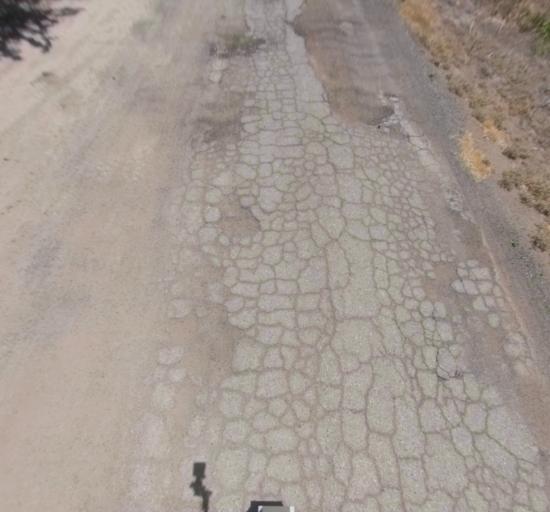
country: US
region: California
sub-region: Madera County
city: Chowchilla
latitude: 36.9962
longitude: -120.3329
